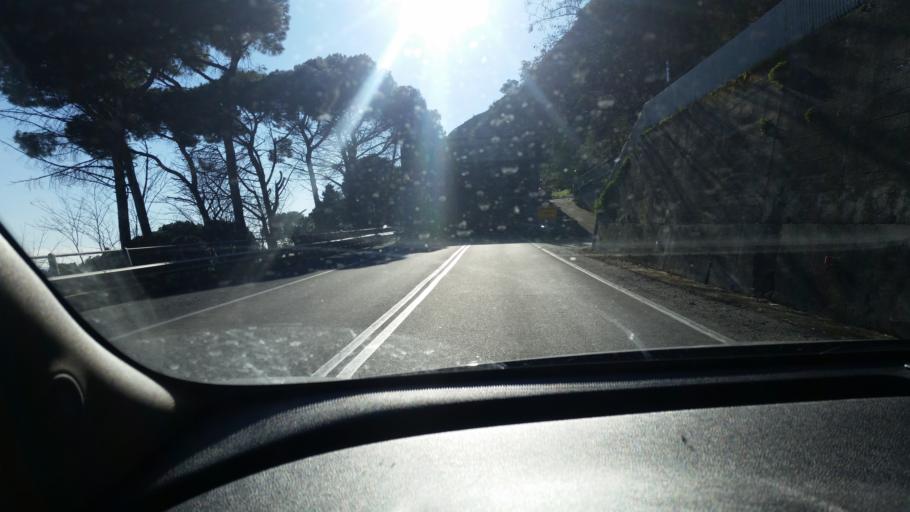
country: IT
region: Calabria
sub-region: Provincia di Catanzaro
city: Squillace Lido
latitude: 38.7665
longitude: 16.5631
